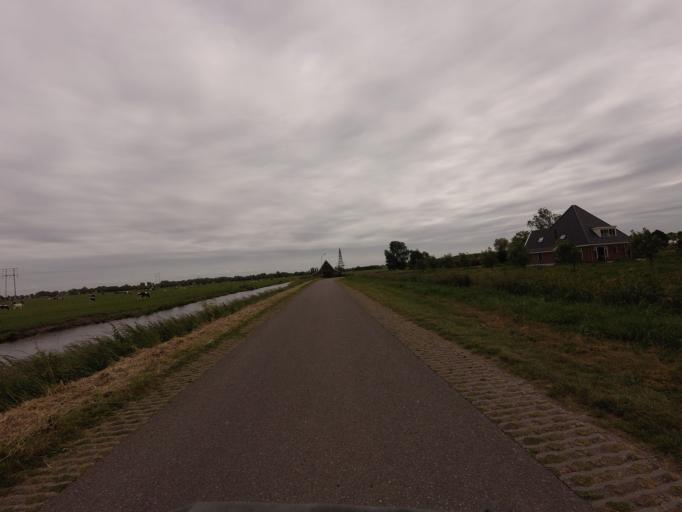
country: NL
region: North Holland
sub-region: Gemeente Medemblik
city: Medemblik
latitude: 52.7561
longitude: 5.1028
